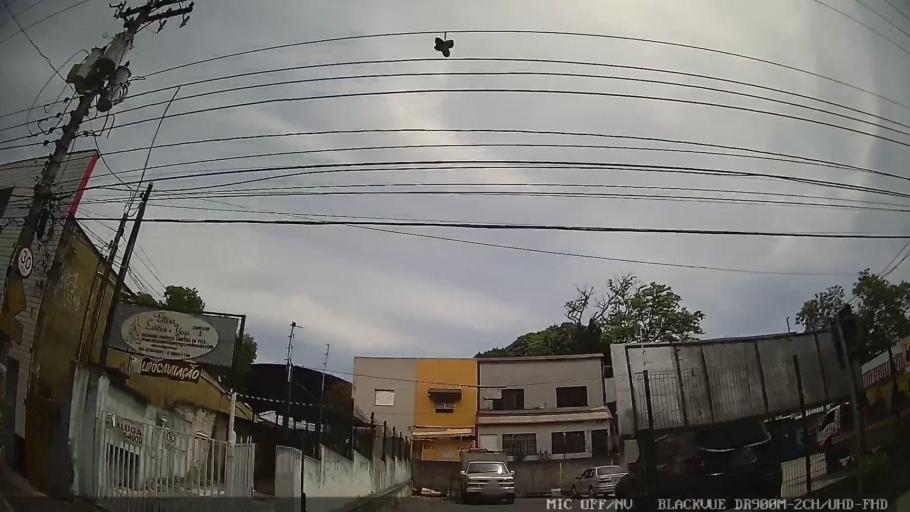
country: BR
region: Sao Paulo
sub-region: Sao Caetano Do Sul
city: Sao Caetano do Sul
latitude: -23.5616
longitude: -46.5407
